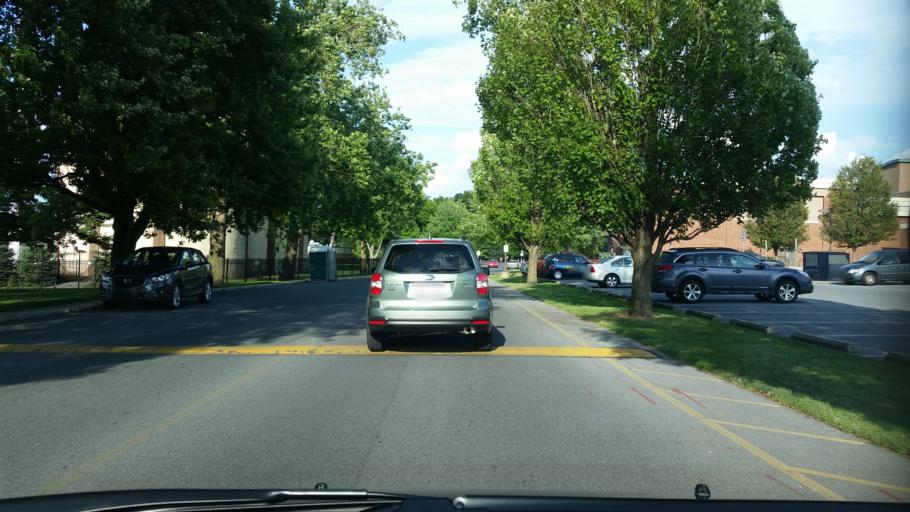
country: US
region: Pennsylvania
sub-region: Lancaster County
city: Lititz
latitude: 40.1568
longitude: -76.3149
